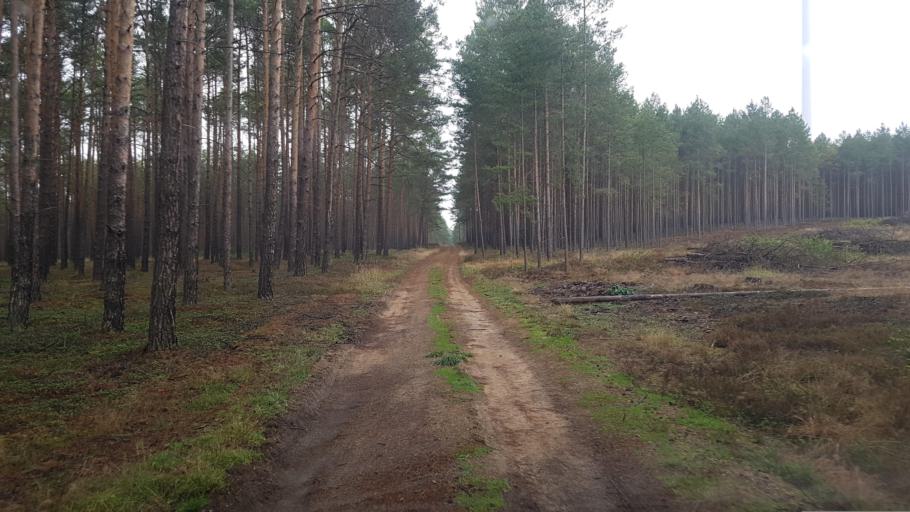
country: DE
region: Brandenburg
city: Sallgast
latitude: 51.6429
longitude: 13.8136
